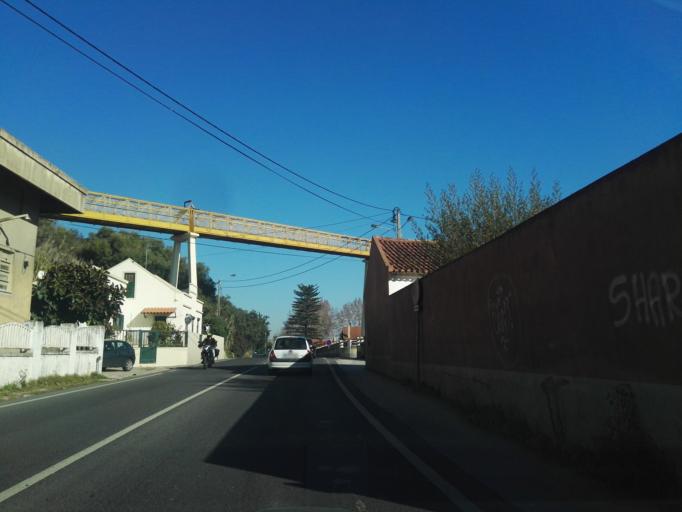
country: PT
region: Lisbon
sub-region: Vila Franca de Xira
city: Alhandra
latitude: 38.9224
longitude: -9.0143
